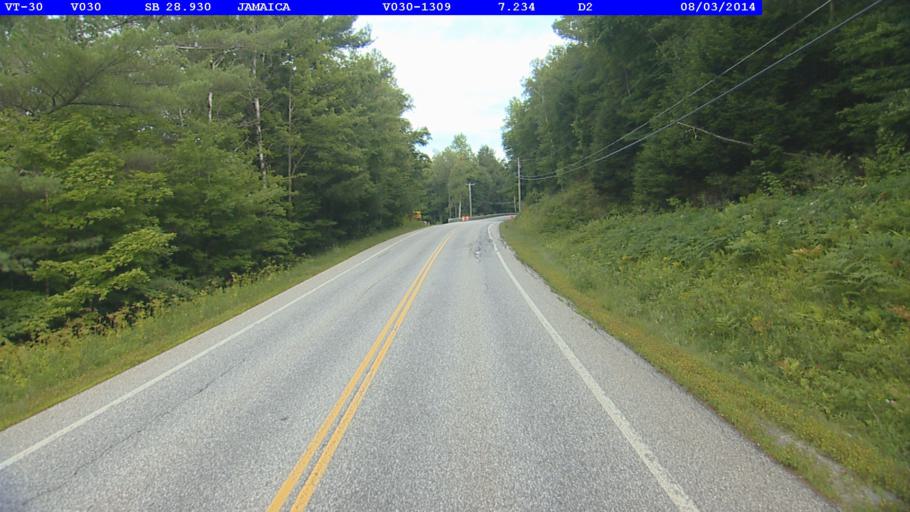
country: US
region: Vermont
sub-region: Windham County
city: Dover
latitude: 43.1335
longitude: -72.8175
